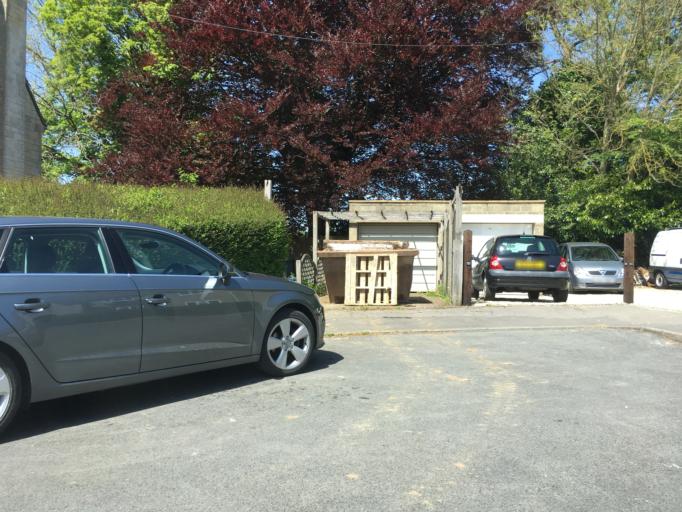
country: GB
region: England
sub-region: Gloucestershire
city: Coates
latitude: 51.7270
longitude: -2.0776
